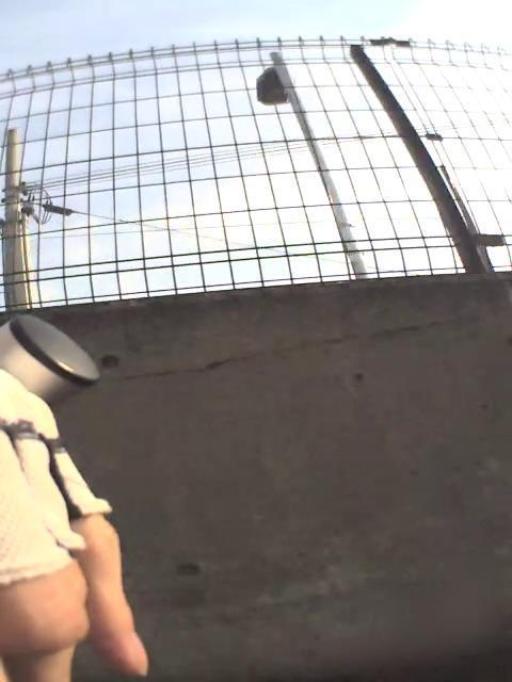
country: JP
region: Osaka
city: Neyagawa
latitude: 34.7387
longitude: 135.6465
